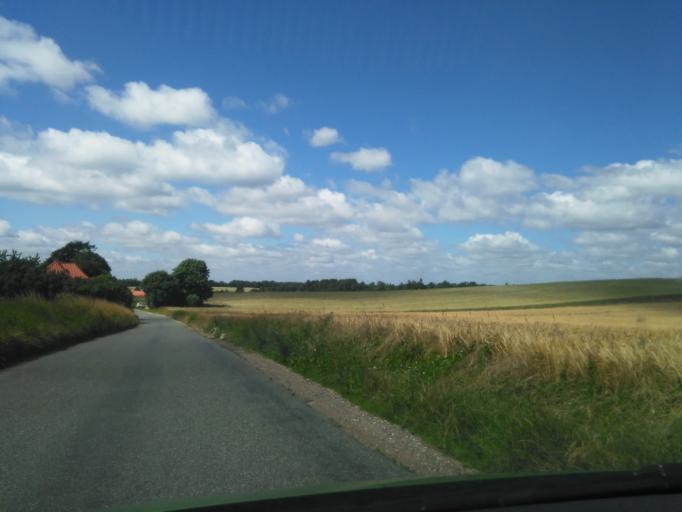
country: DK
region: Central Jutland
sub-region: Arhus Kommune
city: Logten
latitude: 56.1982
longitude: 10.3982
